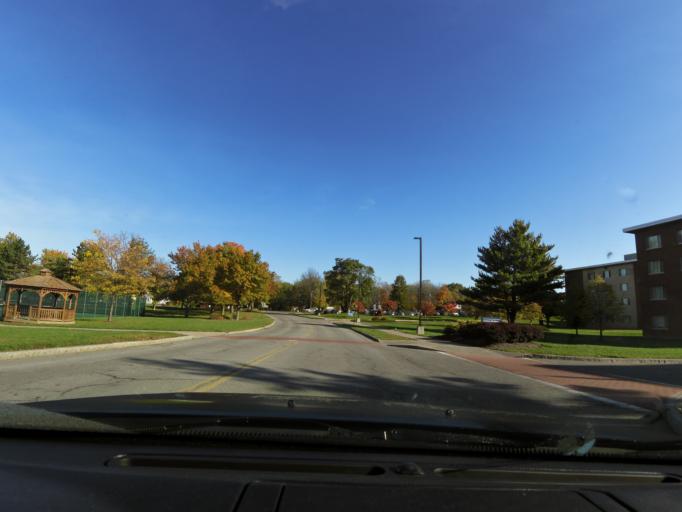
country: US
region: New York
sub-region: Livingston County
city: Geneseo
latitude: 42.8008
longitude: -77.8229
